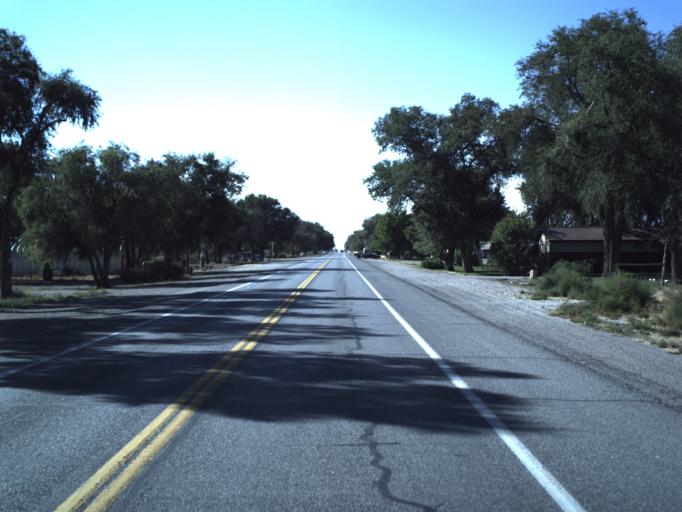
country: US
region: Utah
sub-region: Millard County
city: Delta
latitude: 39.2924
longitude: -112.6527
